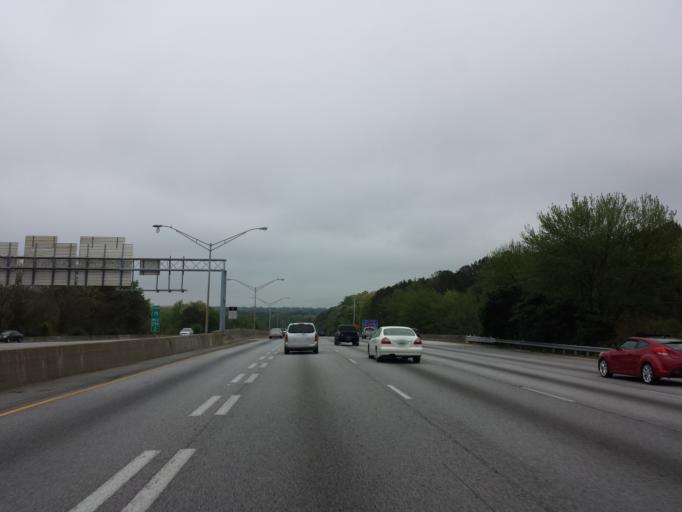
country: US
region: Georgia
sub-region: Cobb County
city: Vinings
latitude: 33.8639
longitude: -84.4387
